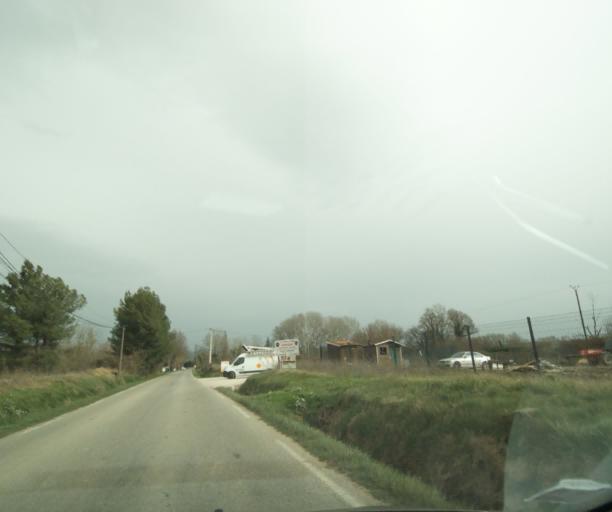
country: FR
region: Provence-Alpes-Cote d'Azur
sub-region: Departement des Bouches-du-Rhone
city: Trets
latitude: 43.4591
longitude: 5.6984
